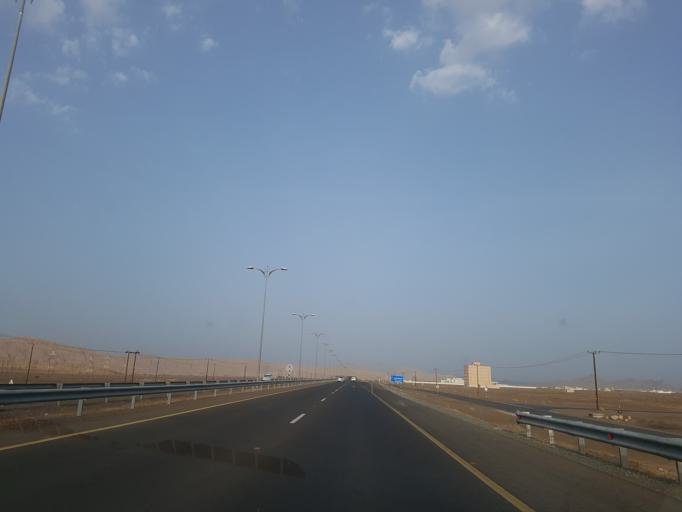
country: OM
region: Al Buraimi
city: Al Buraymi
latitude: 24.2375
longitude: 55.8981
